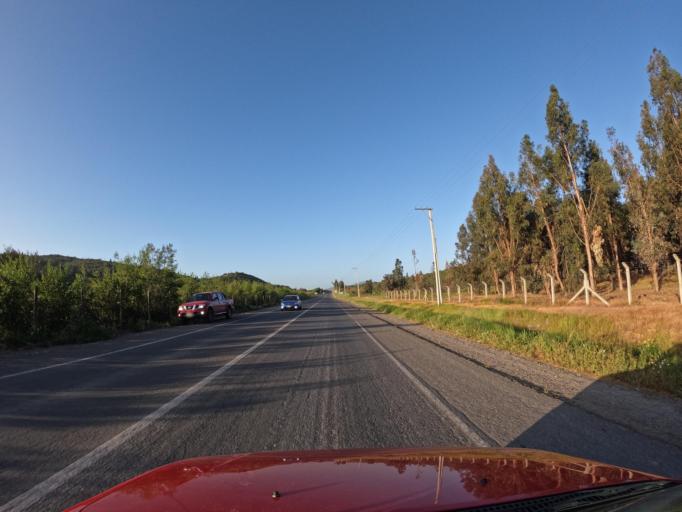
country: CL
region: O'Higgins
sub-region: Provincia de Colchagua
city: Santa Cruz
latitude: -34.3234
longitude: -71.3911
